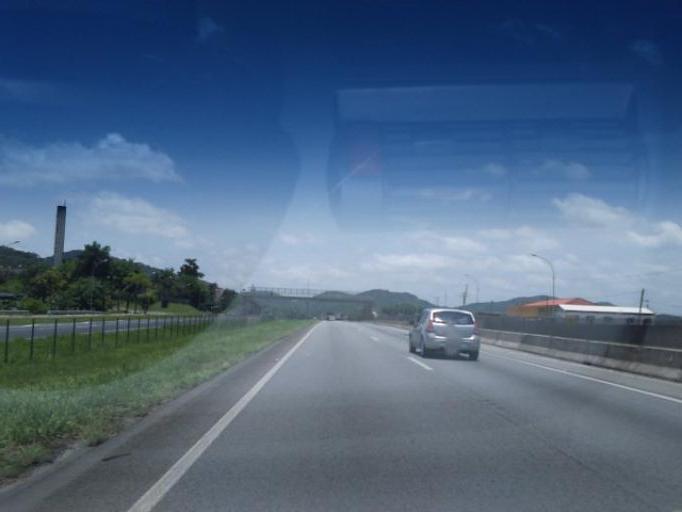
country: BR
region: Sao Paulo
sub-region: Juquia
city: Juquia
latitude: -24.3375
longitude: -47.6435
